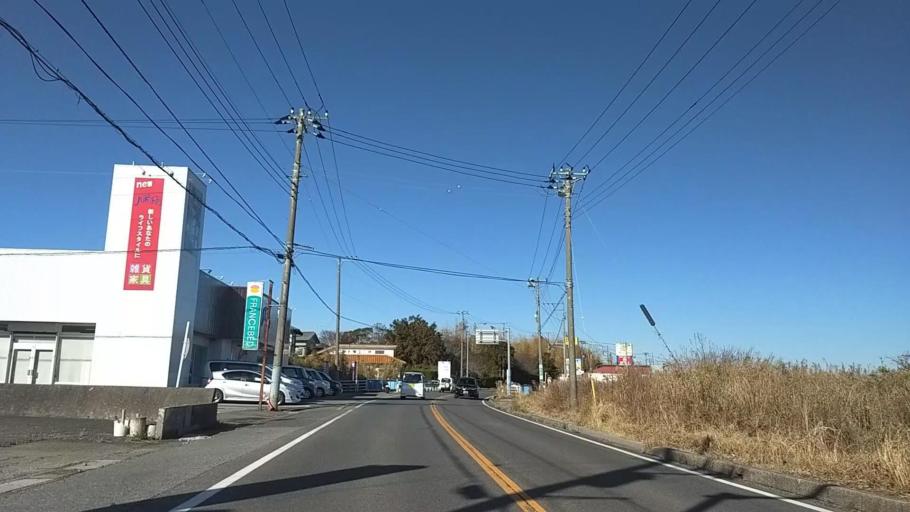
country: JP
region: Chiba
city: Ohara
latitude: 35.2866
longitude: 140.3920
